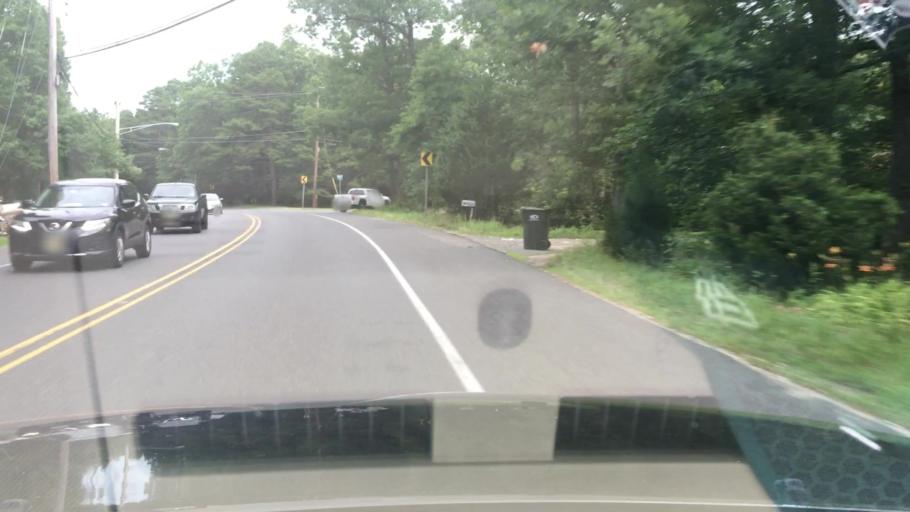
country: US
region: New Jersey
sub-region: Ocean County
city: Cedar Glen West
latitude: 40.0433
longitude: -74.3153
